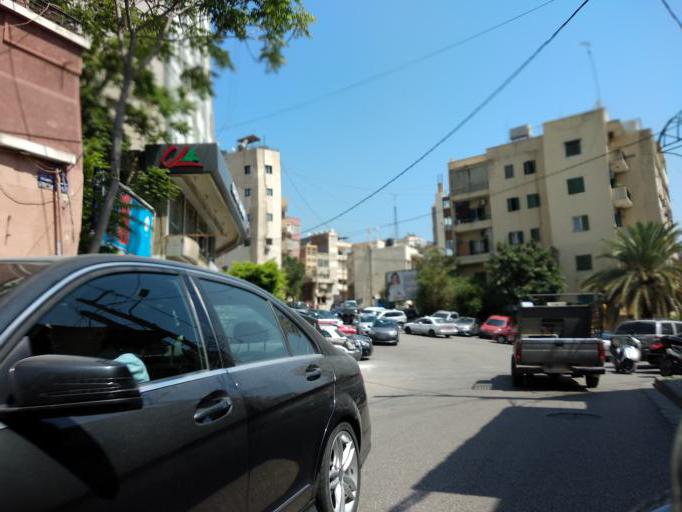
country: LB
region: Mont-Liban
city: Jdaidet el Matn
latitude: 33.8927
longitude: 35.5316
